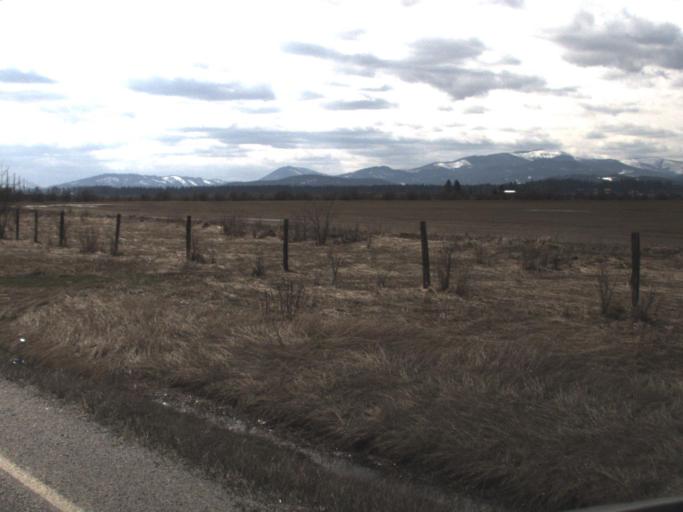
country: US
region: Washington
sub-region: Pend Oreille County
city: Newport
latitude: 48.3760
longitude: -117.3054
